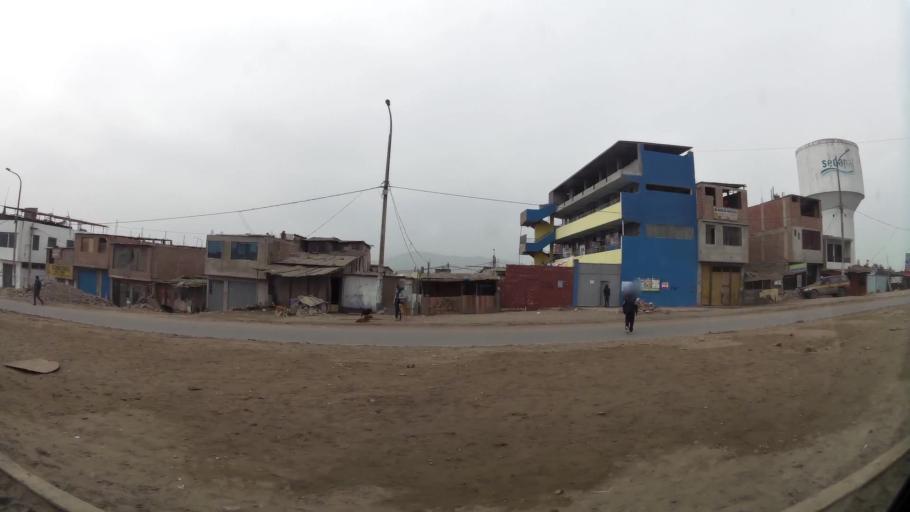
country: PE
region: Lima
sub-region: Lima
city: Surco
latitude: -12.2363
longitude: -76.9396
